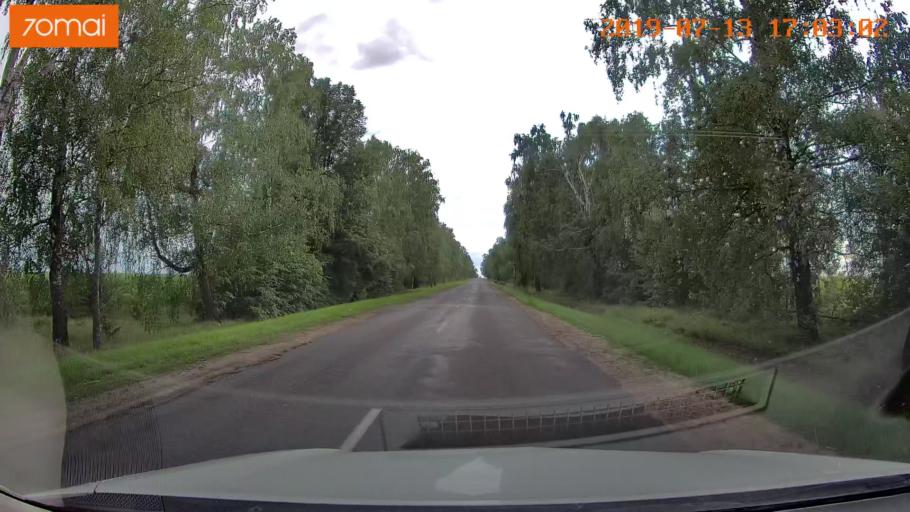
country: BY
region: Mogilev
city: Kirawsk
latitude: 53.2800
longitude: 29.3811
